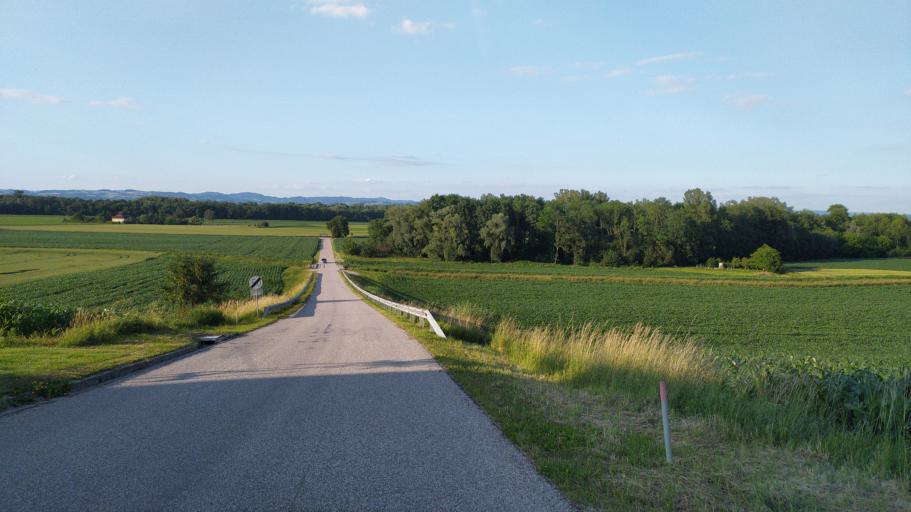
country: AT
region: Lower Austria
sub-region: Politischer Bezirk Amstetten
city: Strengberg
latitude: 48.1695
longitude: 14.6248
